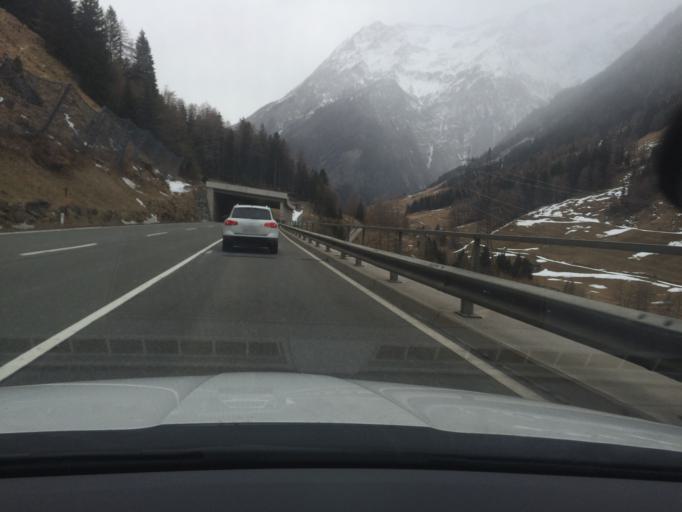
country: AT
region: Tyrol
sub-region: Politischer Bezirk Lienz
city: Matrei in Osttirol
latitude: 47.0655
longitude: 12.5307
